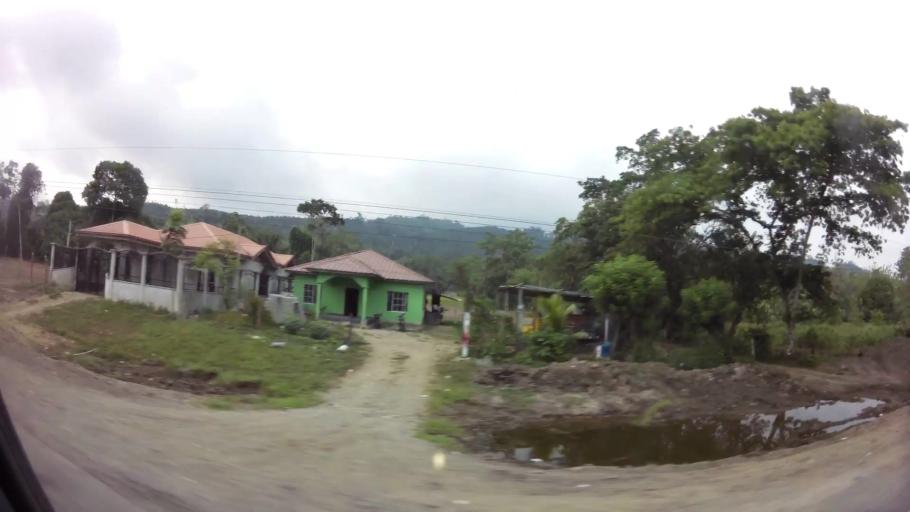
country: HN
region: Yoro
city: Guaimitas
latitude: 15.4956
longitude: -87.7183
